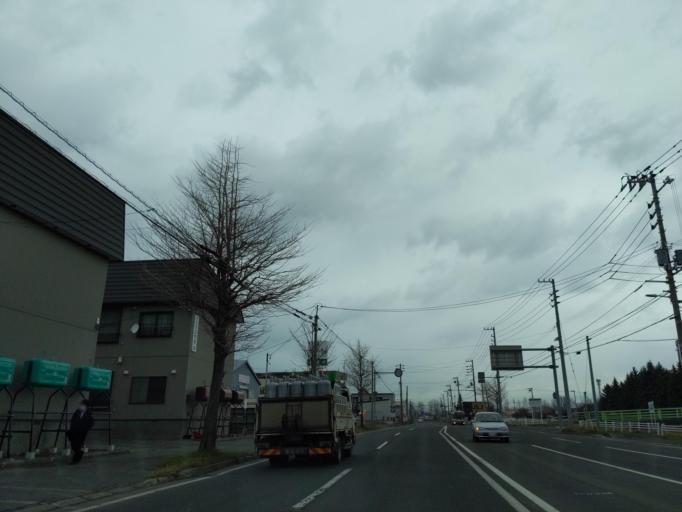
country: JP
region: Hokkaido
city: Ishikari
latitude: 43.1529
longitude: 141.3605
